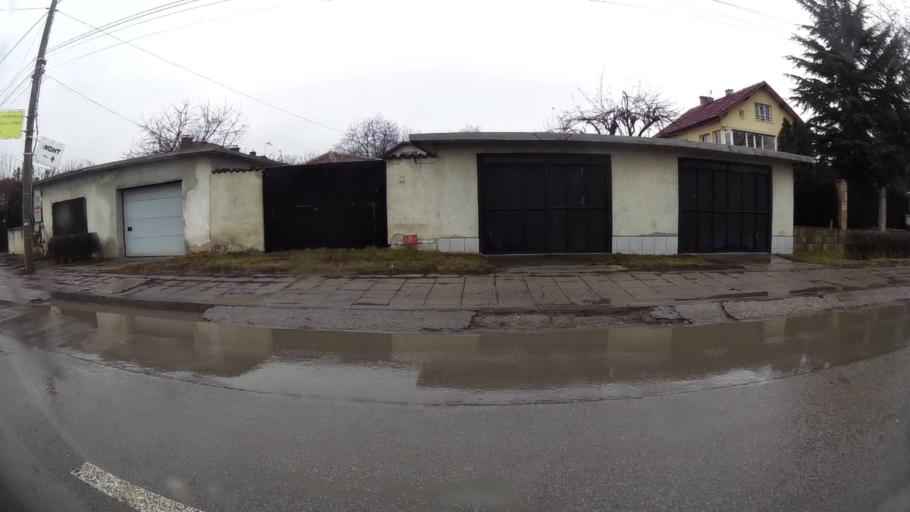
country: BG
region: Sofia-Capital
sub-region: Stolichna Obshtina
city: Sofia
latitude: 42.6339
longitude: 23.4090
